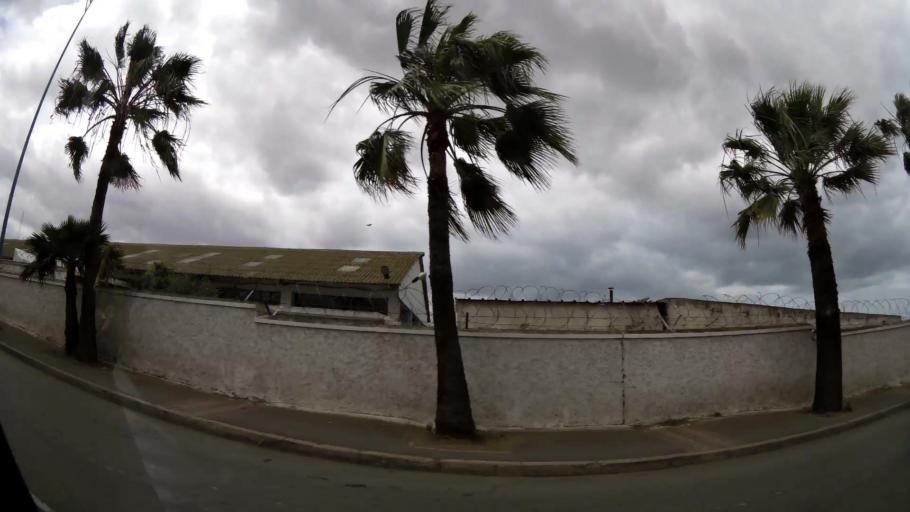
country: MA
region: Grand Casablanca
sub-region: Casablanca
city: Casablanca
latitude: 33.5914
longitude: -7.5458
